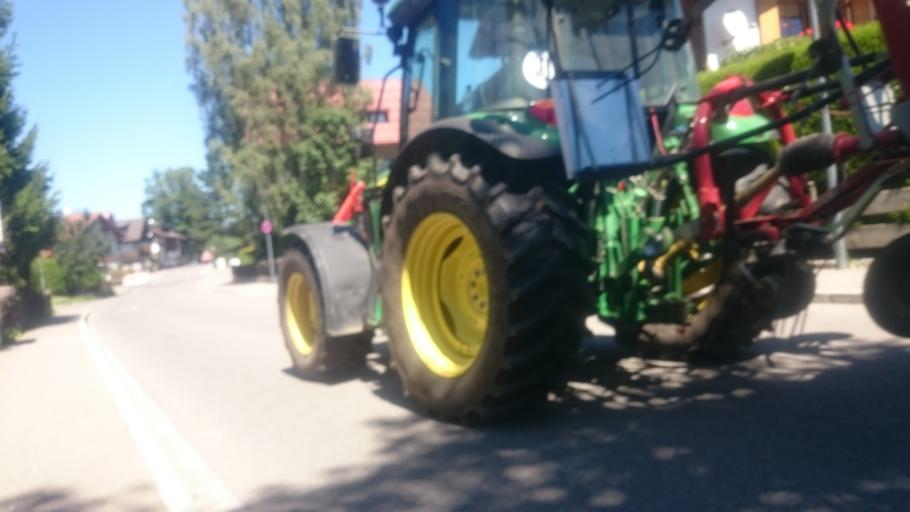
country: DE
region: Bavaria
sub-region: Swabia
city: Oberstdorf
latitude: 47.4029
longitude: 10.2783
